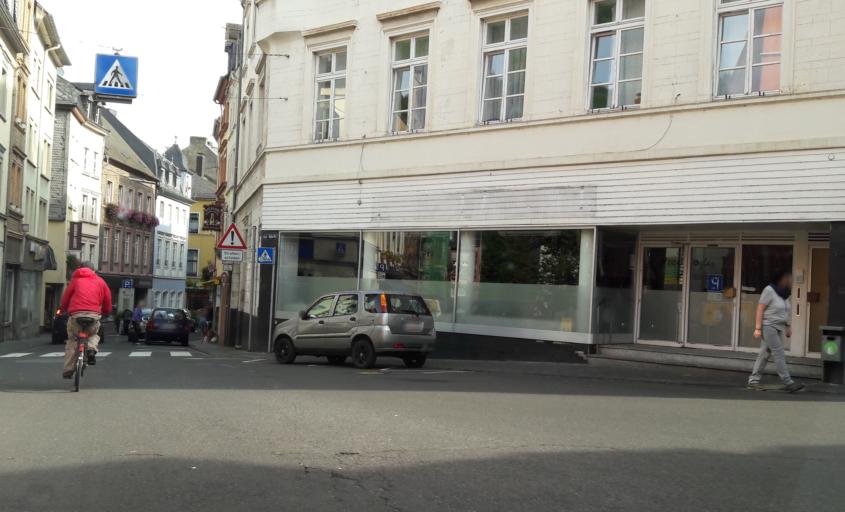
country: DE
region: Rheinland-Pfalz
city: Traben-Trarbach
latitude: 49.9475
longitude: 7.1115
